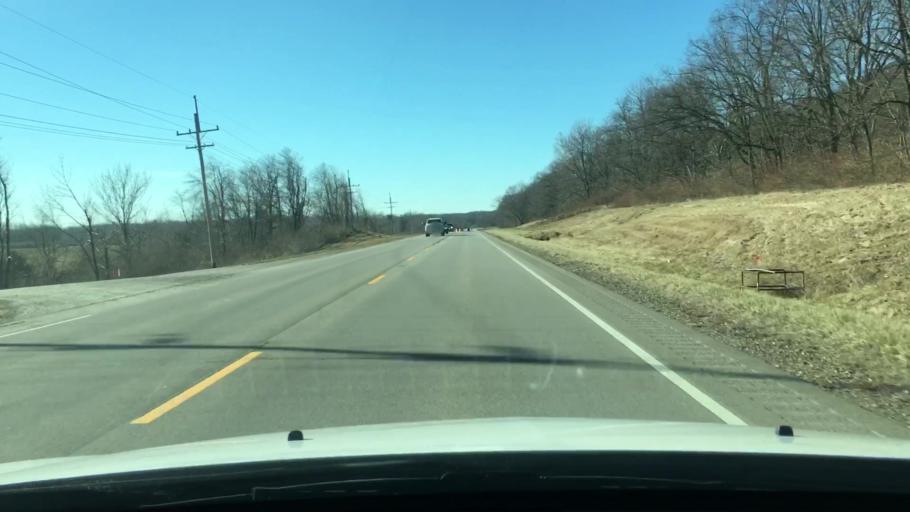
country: US
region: Illinois
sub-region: Peoria County
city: Glasford
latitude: 40.5215
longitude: -89.8869
